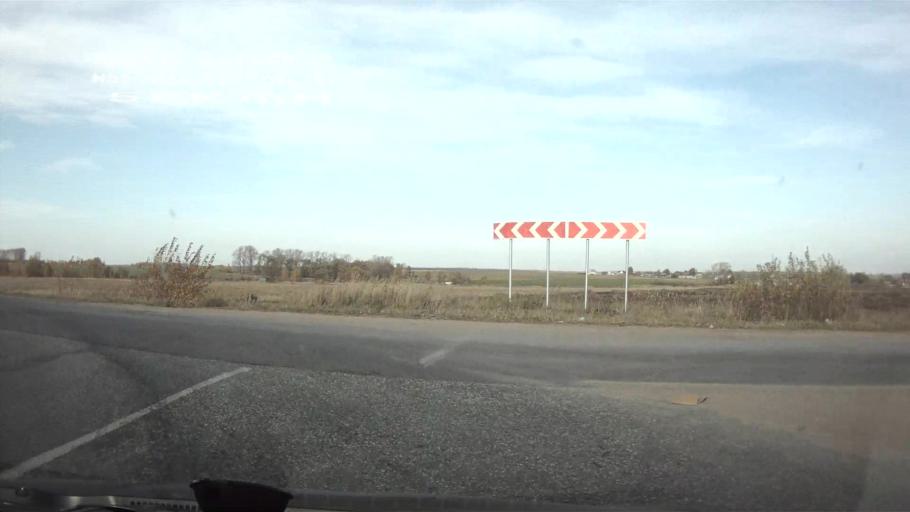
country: RU
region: Chuvashia
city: Ibresi
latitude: 55.2858
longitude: 47.0803
